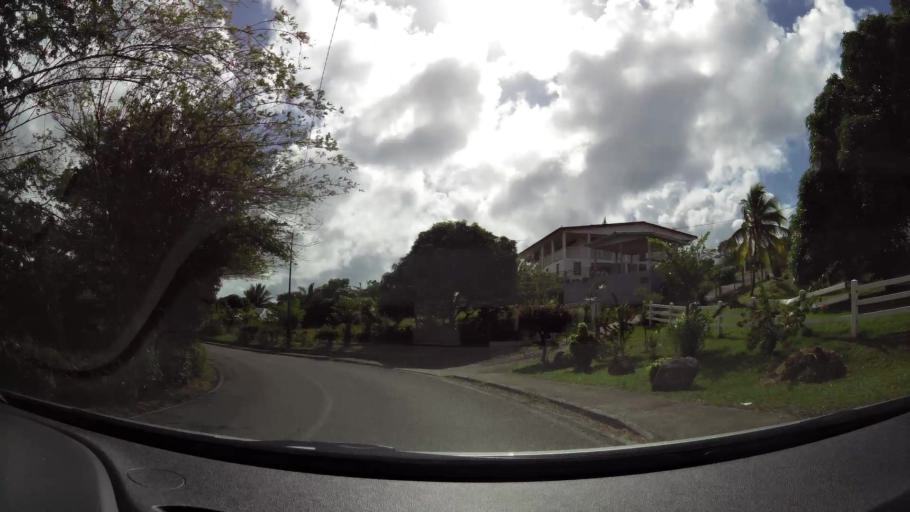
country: MQ
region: Martinique
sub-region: Martinique
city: Les Trois-Ilets
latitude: 14.4809
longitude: -61.0155
